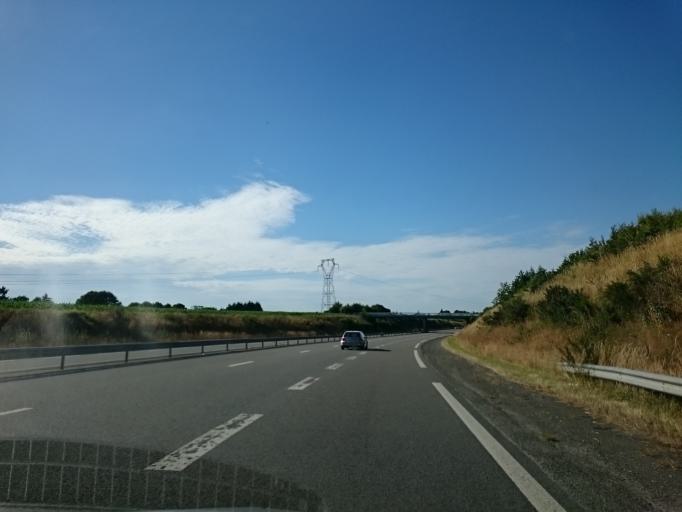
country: FR
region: Brittany
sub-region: Departement d'Ille-et-Vilaine
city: Corps-Nuds
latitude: 47.9925
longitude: -1.5913
